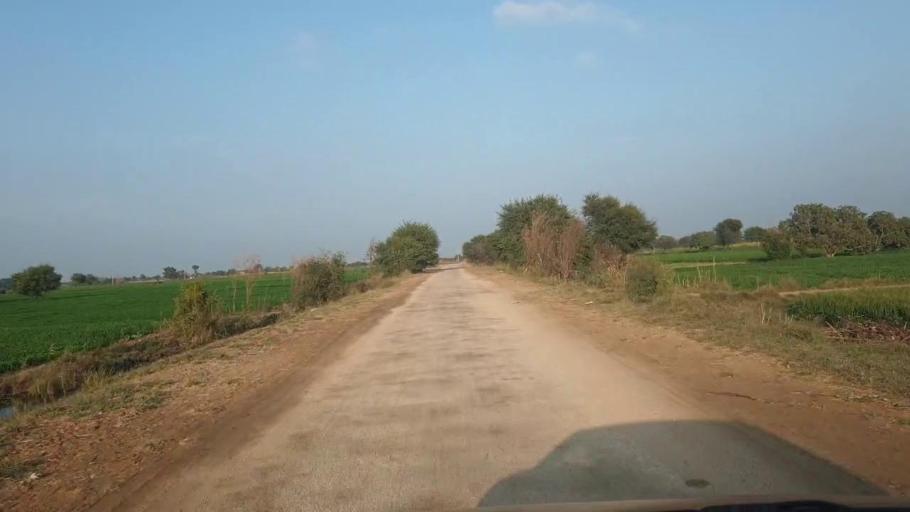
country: PK
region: Sindh
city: Berani
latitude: 25.8553
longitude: 68.7343
